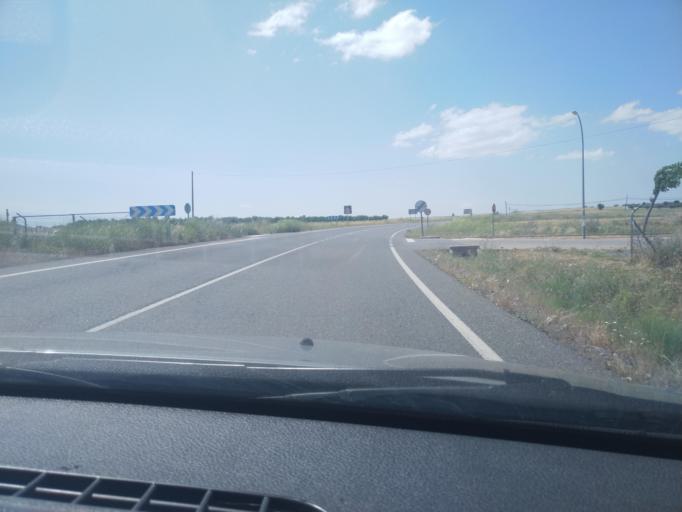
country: ES
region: Castille-La Mancha
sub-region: Province of Toledo
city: Casasbuenas
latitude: 39.7601
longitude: -4.1308
